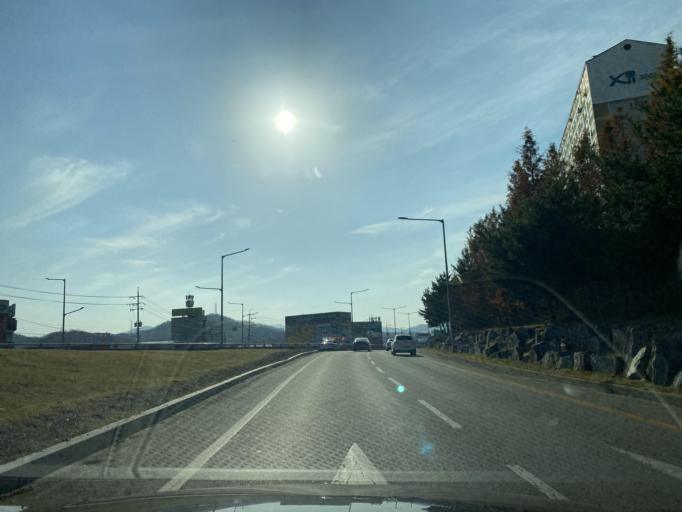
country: KR
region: Chungcheongnam-do
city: Cheonan
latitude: 36.7865
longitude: 127.1175
